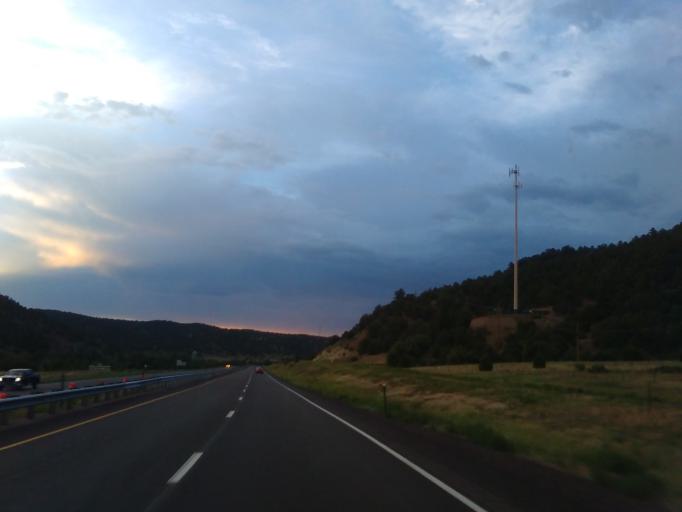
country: US
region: Colorado
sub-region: Las Animas County
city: Trinidad
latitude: 37.0968
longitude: -104.5196
